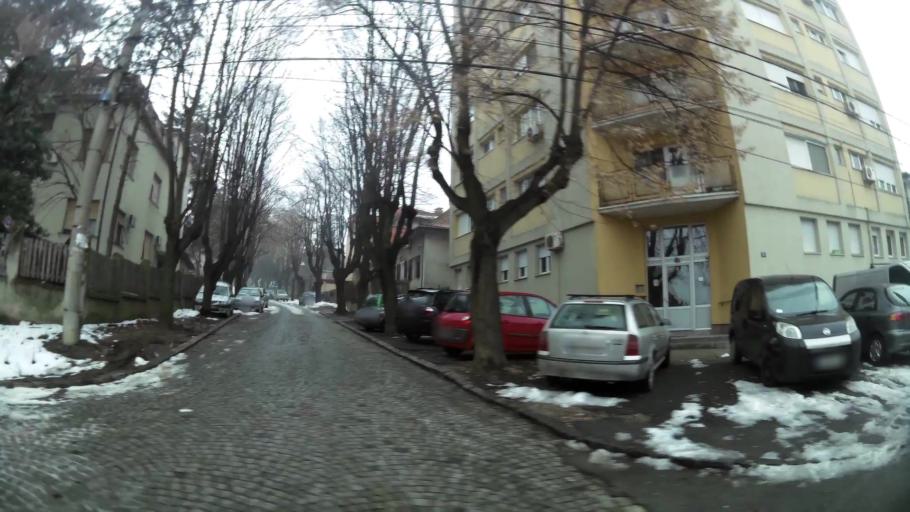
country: RS
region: Central Serbia
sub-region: Belgrade
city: Savski Venac
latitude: 44.7927
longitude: 20.4405
